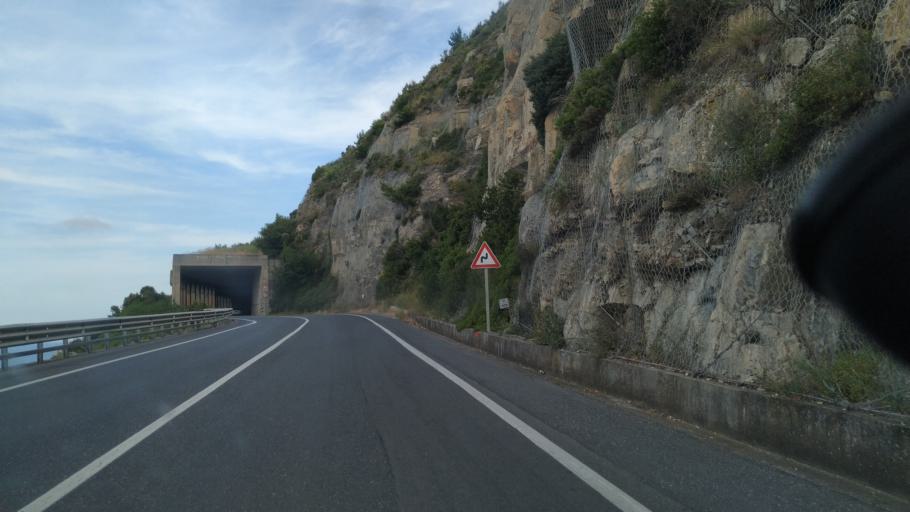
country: IT
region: Liguria
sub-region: Provincia di Savona
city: Marina di Andora
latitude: 43.9609
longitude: 8.1694
